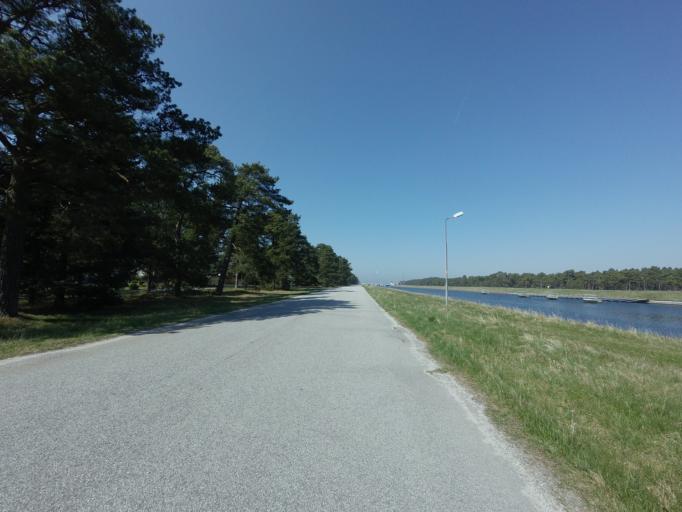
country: SE
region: Skane
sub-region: Vellinge Kommun
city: Ljunghusen
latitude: 55.4021
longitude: 12.9405
